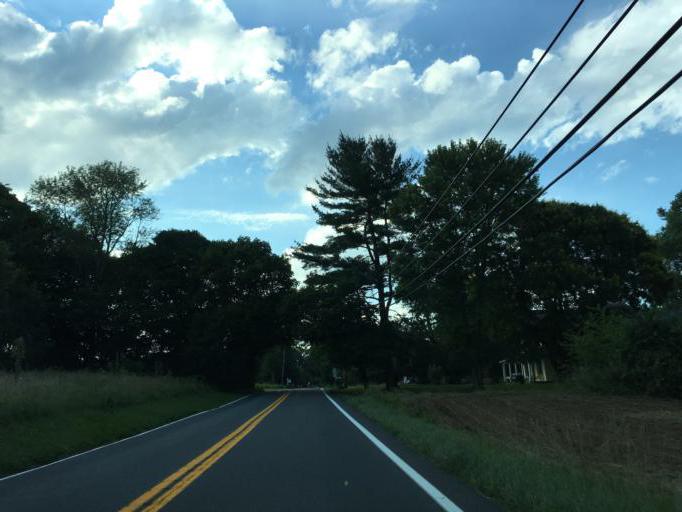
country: US
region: Maryland
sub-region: Harford County
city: Fallston
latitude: 39.4975
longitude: -76.4721
